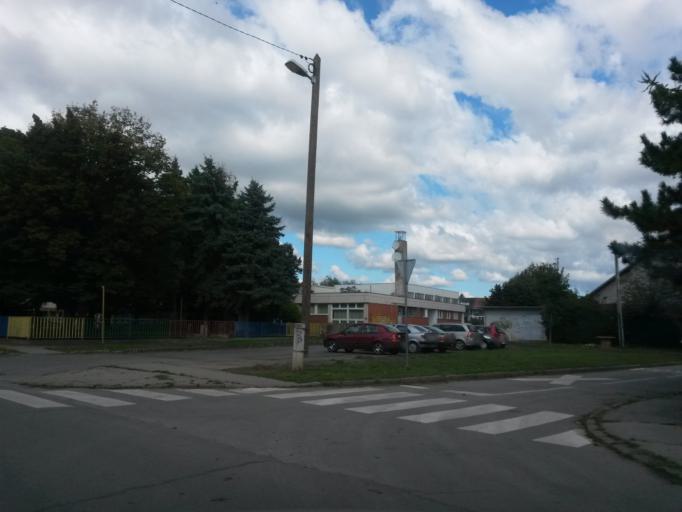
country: HR
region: Osjecko-Baranjska
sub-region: Grad Osijek
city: Osijek
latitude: 45.5567
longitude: 18.7304
